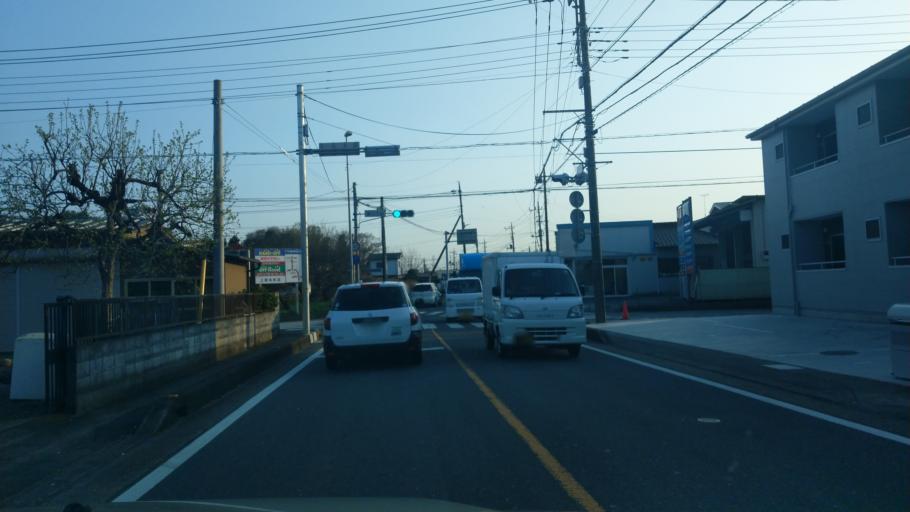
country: JP
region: Saitama
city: Ageoshimo
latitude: 36.0035
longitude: 139.6053
